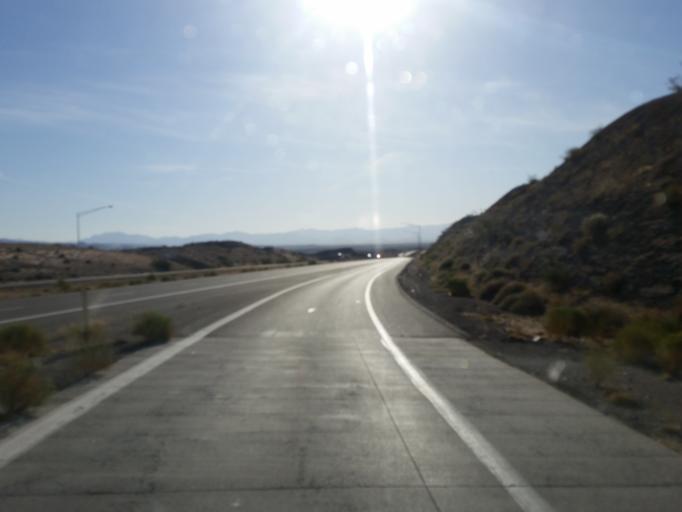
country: US
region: Arizona
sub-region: Mohave County
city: Desert Hills
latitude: 34.7239
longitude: -114.4172
